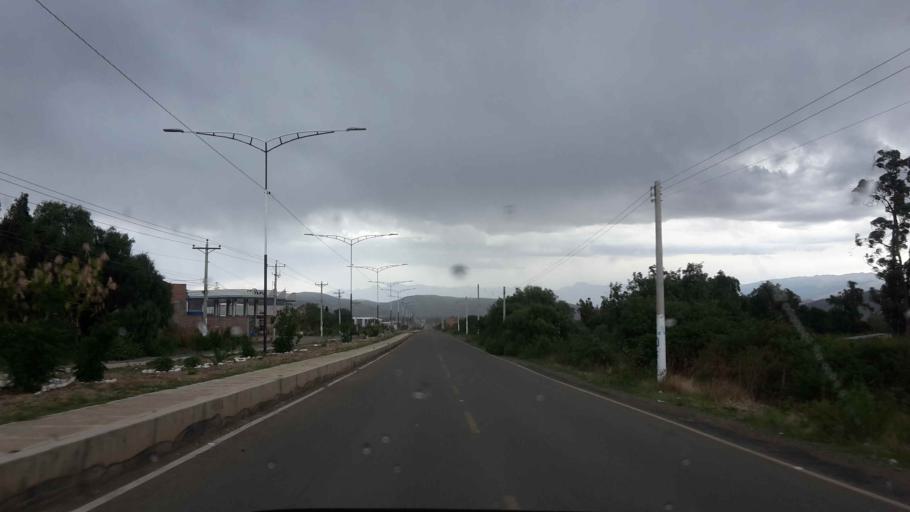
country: BO
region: Cochabamba
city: Tarata
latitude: -17.6040
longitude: -66.0318
